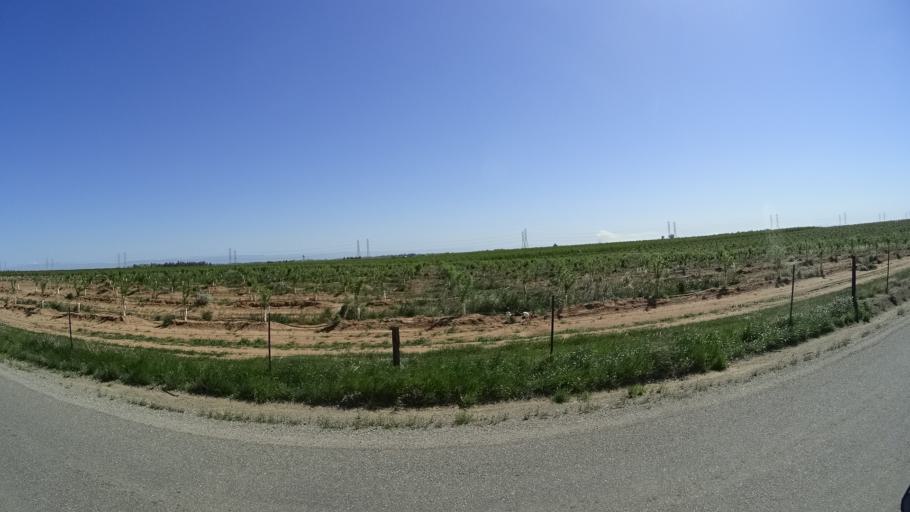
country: US
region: California
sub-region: Glenn County
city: Orland
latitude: 39.6766
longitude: -122.2716
